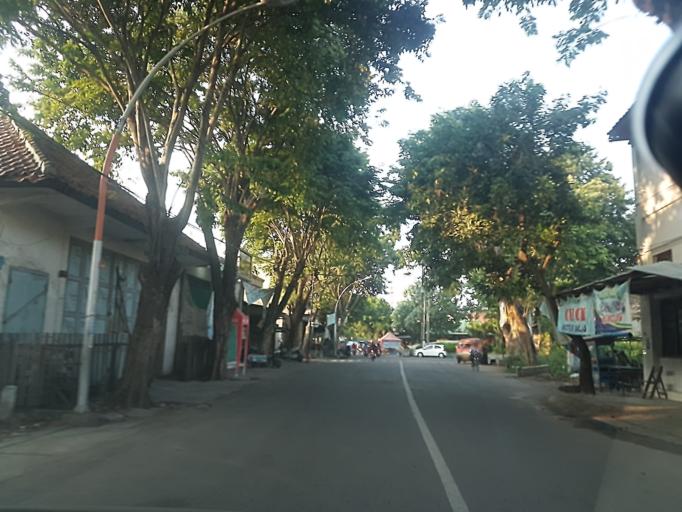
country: ID
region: East Java
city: Gresik
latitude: -7.1542
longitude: 112.6582
